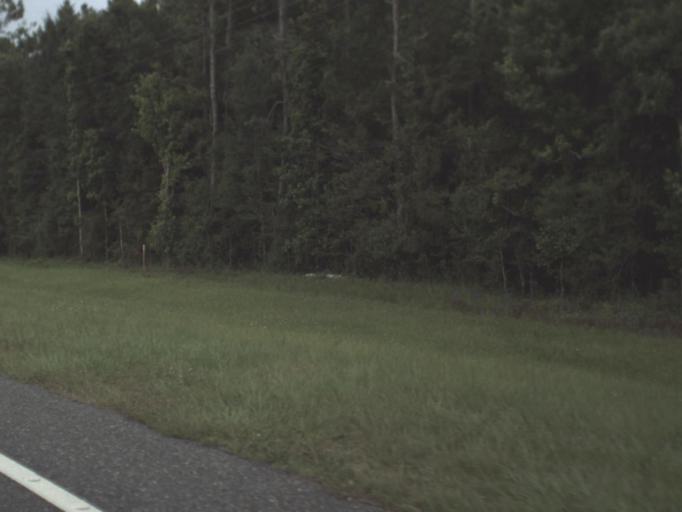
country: US
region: Florida
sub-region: Levy County
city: Williston Highlands
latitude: 29.2359
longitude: -82.7128
